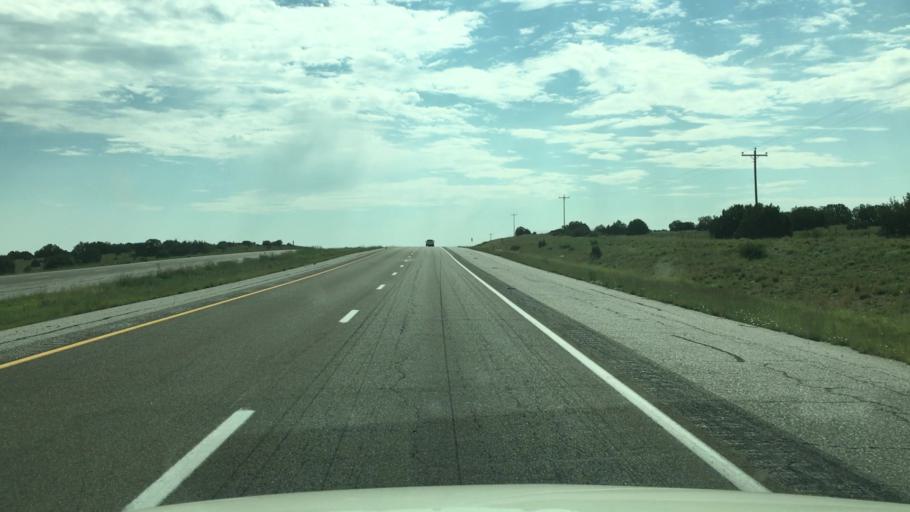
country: US
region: New Mexico
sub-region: Torrance County
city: Moriarty
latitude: 34.9974
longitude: -105.4213
